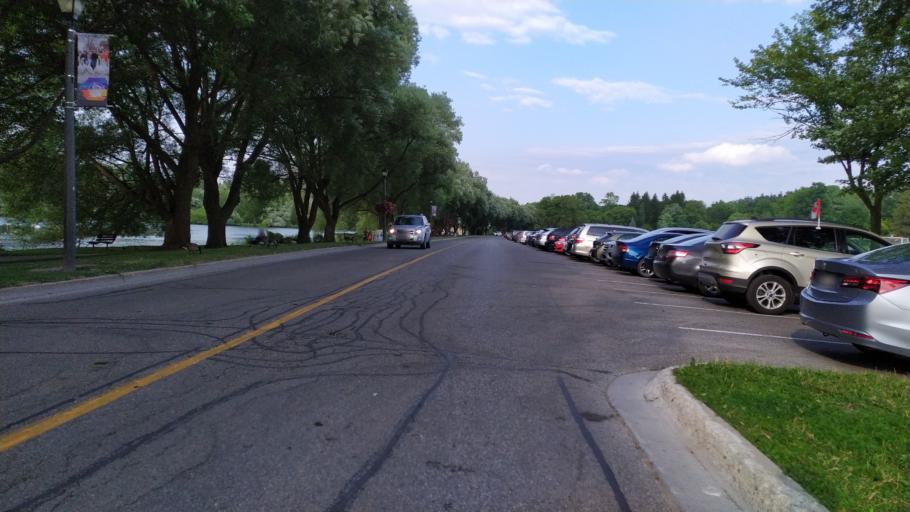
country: CA
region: Ontario
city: Stratford
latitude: 43.3755
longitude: -80.9697
